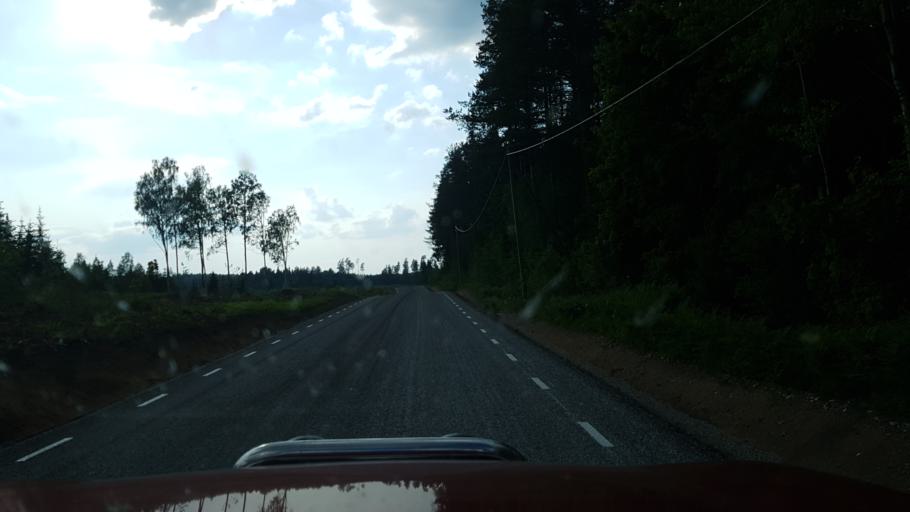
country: EE
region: Tartu
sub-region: UElenurme vald
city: Ulenurme
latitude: 58.1084
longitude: 26.7482
